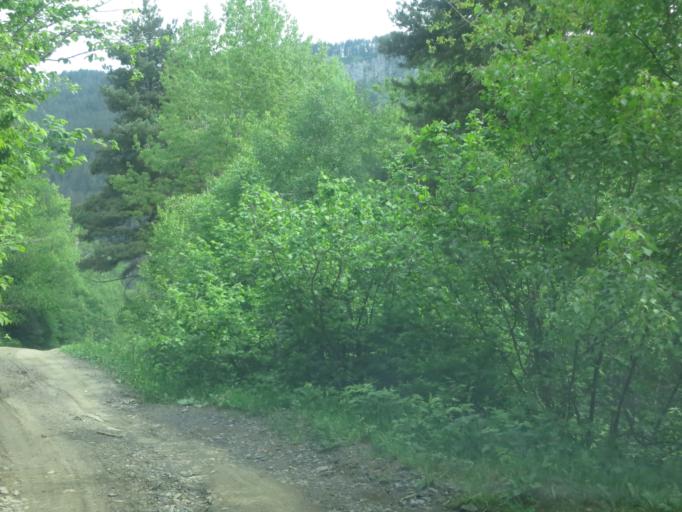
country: RU
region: Chechnya
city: Itum-Kali
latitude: 42.3656
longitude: 45.6428
